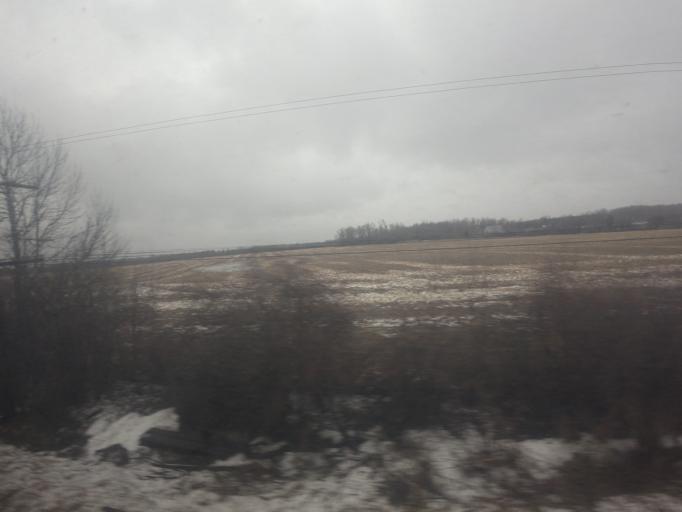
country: CA
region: Ontario
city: Deseronto
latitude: 44.2265
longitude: -77.1029
